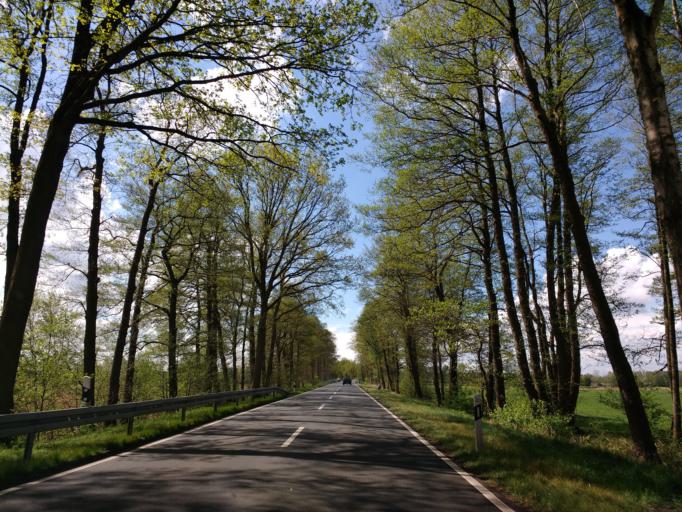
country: DE
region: Lower Saxony
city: Essel
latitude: 52.7245
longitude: 9.6890
